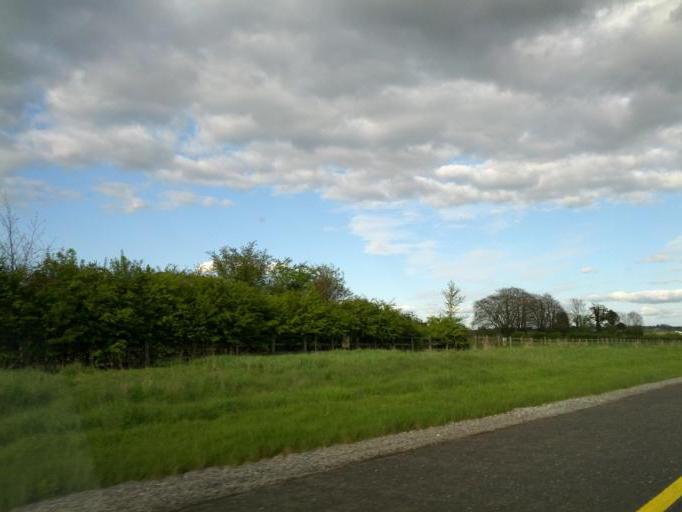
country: IE
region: Leinster
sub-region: An Mhi
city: Enfield
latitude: 53.4045
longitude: -6.8243
